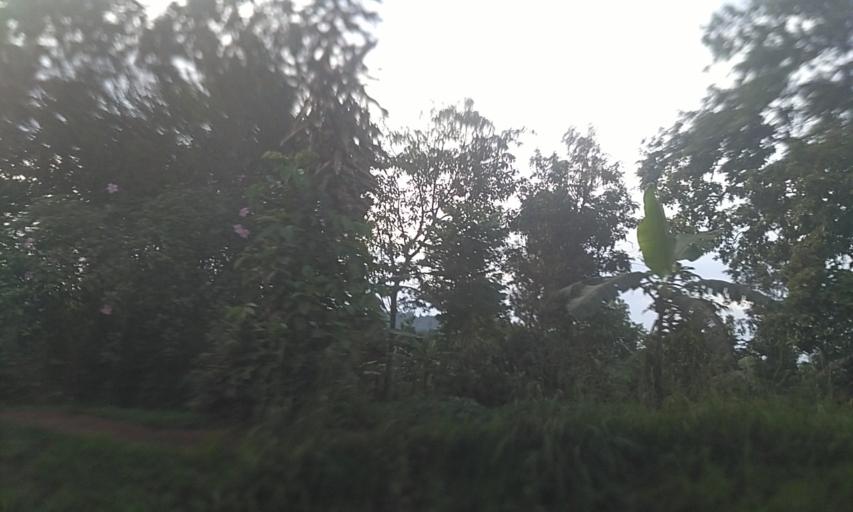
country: UG
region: Central Region
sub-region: Wakiso District
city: Kajansi
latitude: 0.2462
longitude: 32.5007
